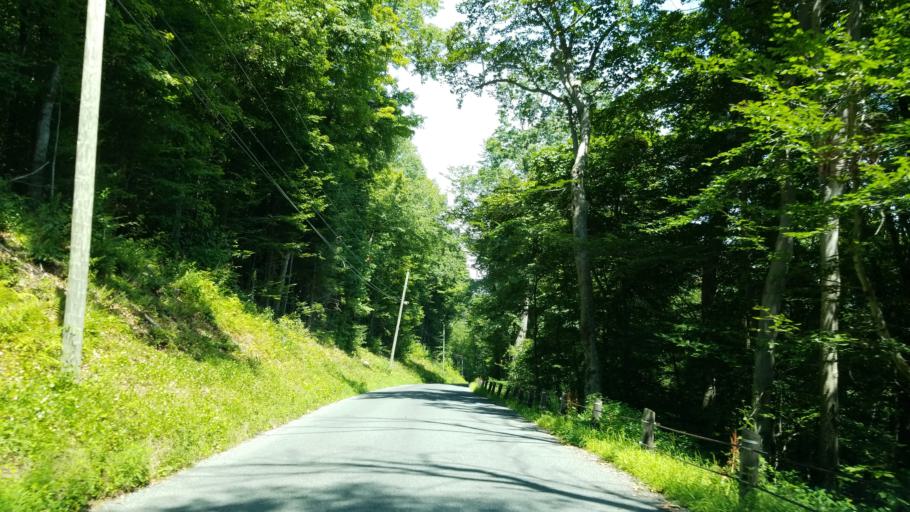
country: US
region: Connecticut
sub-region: Litchfield County
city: Winchester Center
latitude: 41.9247
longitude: -73.2107
